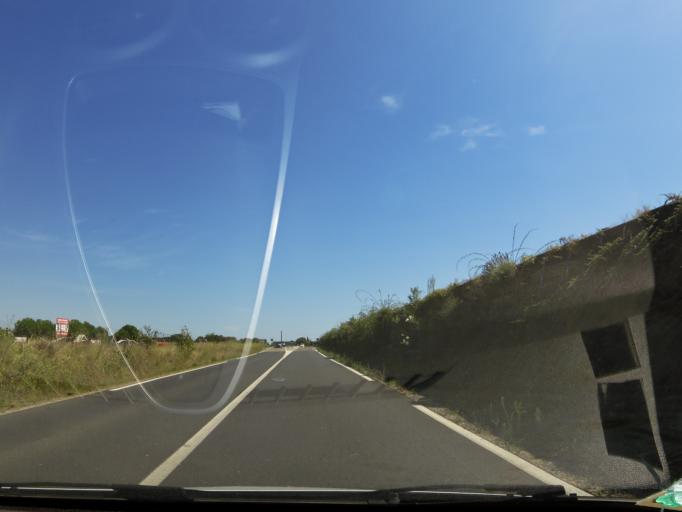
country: FR
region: Languedoc-Roussillon
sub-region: Departement de l'Herault
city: Vendargues
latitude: 43.6605
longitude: 3.9797
